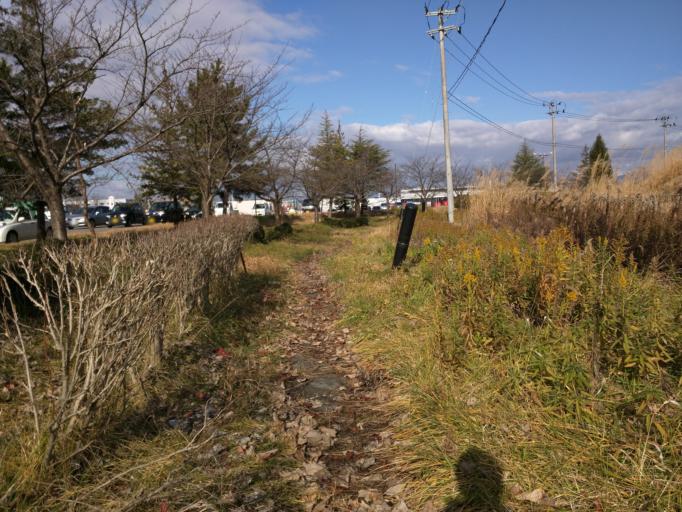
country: JP
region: Fukushima
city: Kitakata
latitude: 37.5231
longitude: 139.9162
